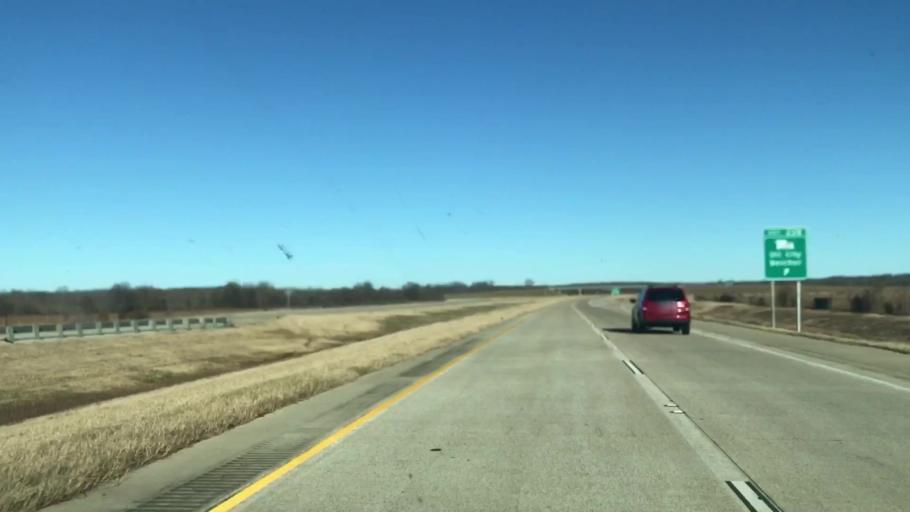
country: US
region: Louisiana
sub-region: Caddo Parish
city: Oil City
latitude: 32.7608
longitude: -93.8860
